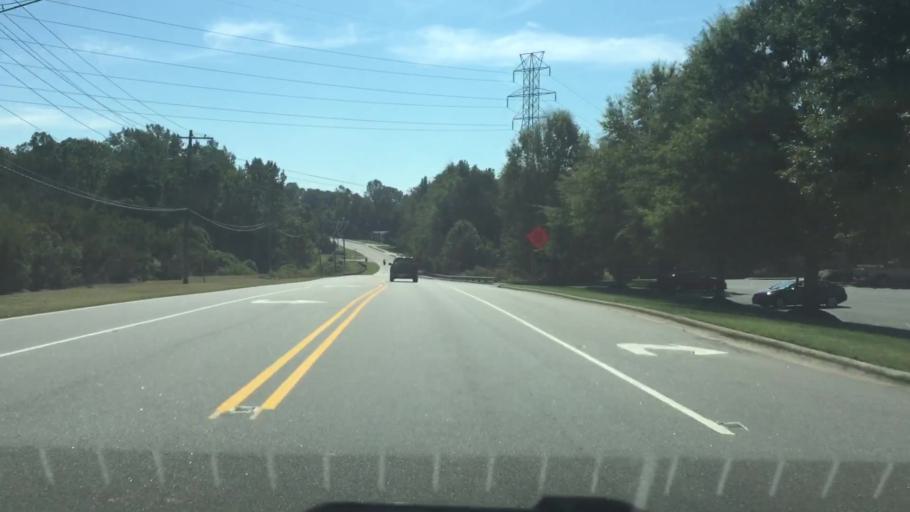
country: US
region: North Carolina
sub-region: Iredell County
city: Mooresville
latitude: 35.5940
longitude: -80.8160
